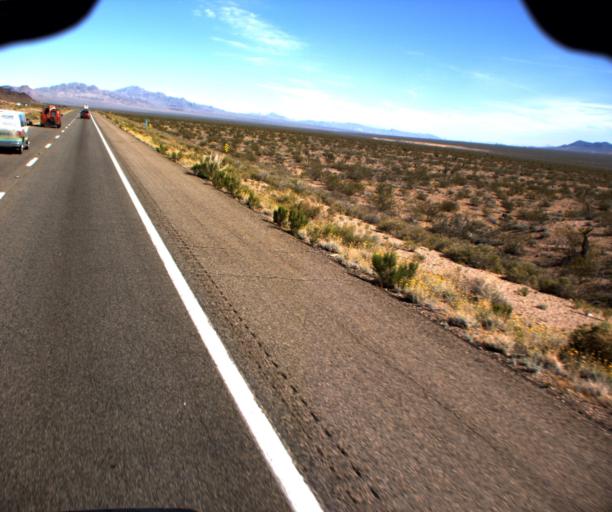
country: US
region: Arizona
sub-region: Mohave County
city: Dolan Springs
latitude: 35.7600
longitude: -114.5068
